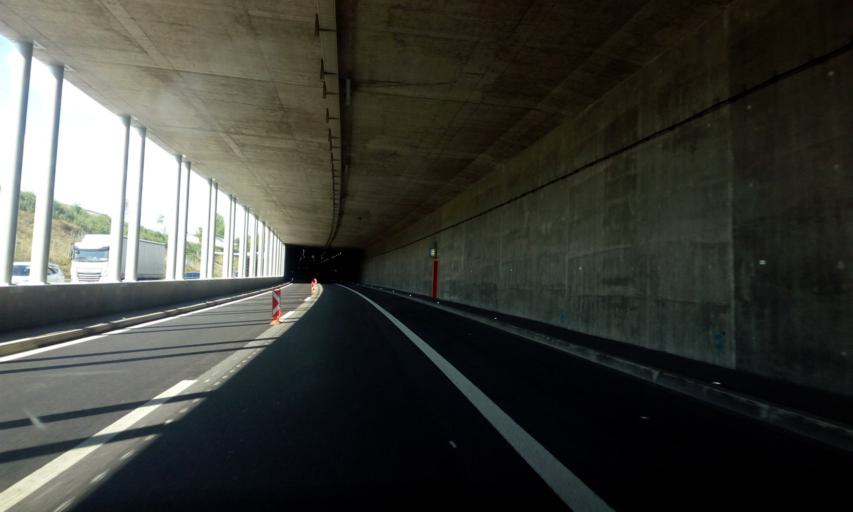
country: CH
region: Fribourg
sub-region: See District
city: Murten
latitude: 46.9197
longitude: 7.1288
